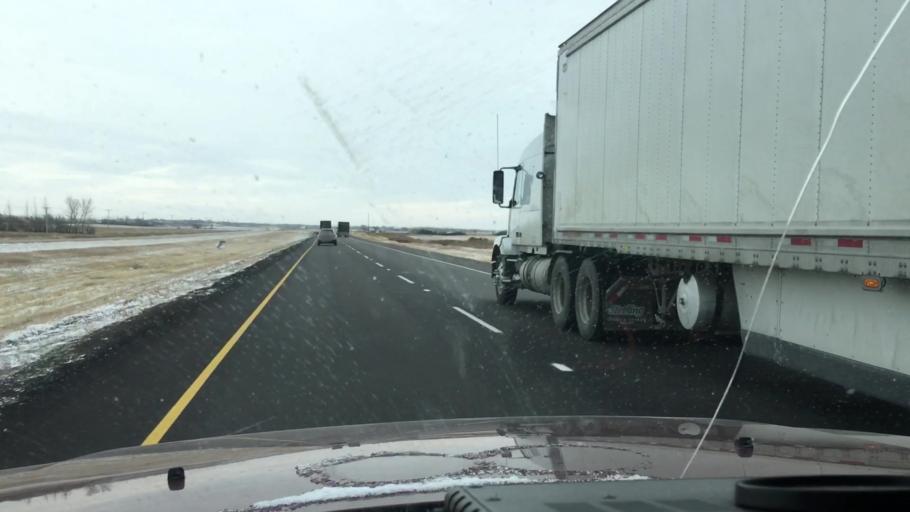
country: CA
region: Saskatchewan
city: Saskatoon
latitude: 51.7888
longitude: -106.4823
